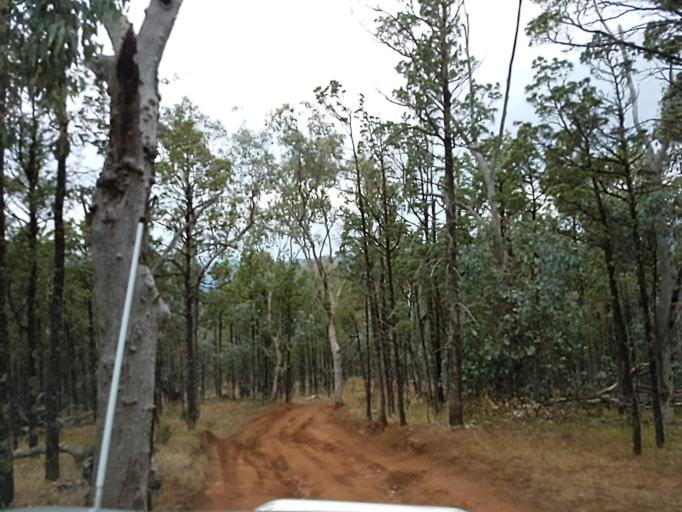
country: AU
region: New South Wales
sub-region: Snowy River
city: Jindabyne
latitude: -36.9293
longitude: 148.3881
